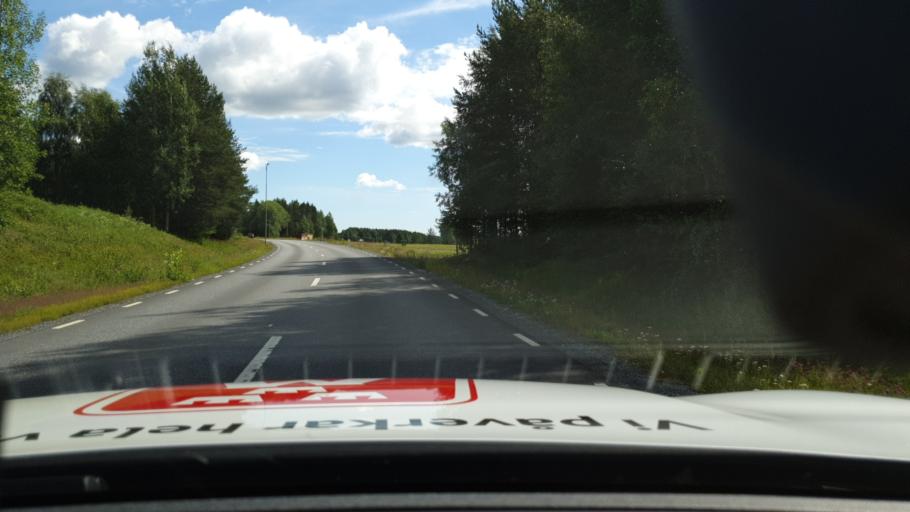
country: SE
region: Norrbotten
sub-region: Lulea Kommun
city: Gammelstad
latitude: 65.8035
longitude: 22.0375
